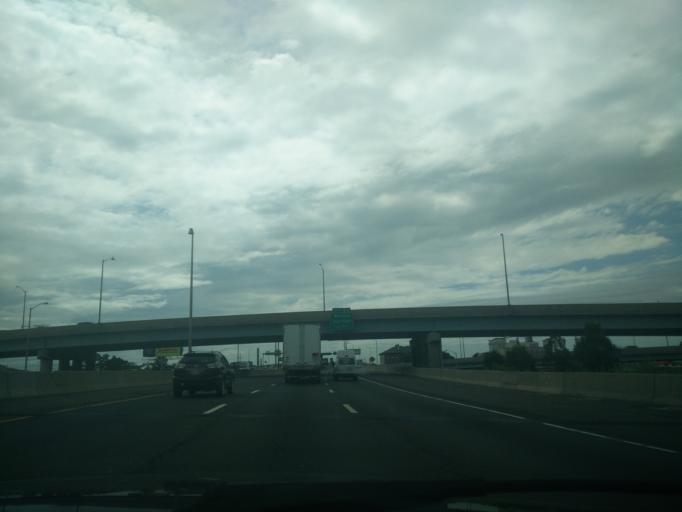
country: US
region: Connecticut
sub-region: Fairfield County
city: Bridgeport
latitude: 41.1717
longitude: -73.1915
